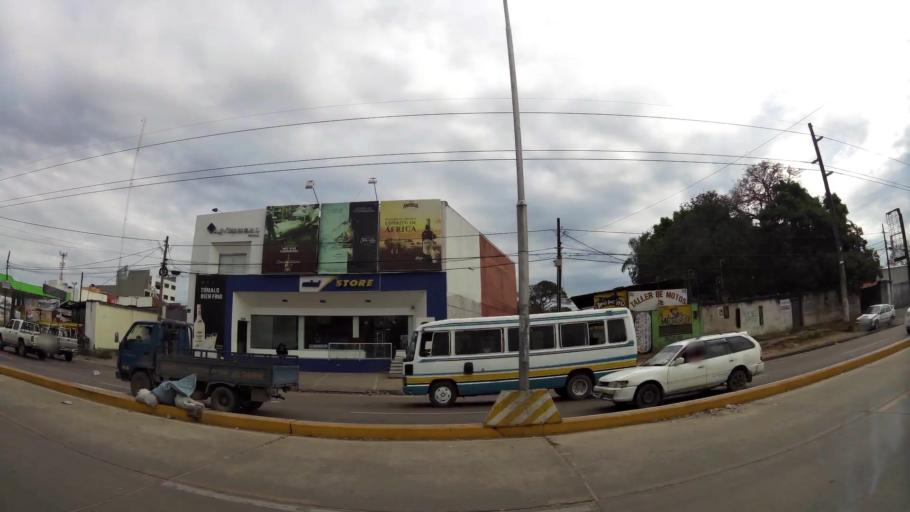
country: BO
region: Santa Cruz
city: Santa Cruz de la Sierra
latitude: -17.8030
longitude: -63.1997
